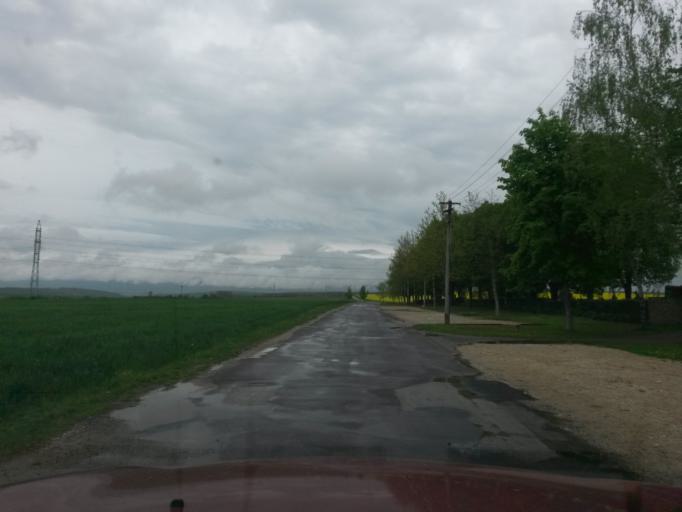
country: SK
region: Kosicky
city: Moldava nad Bodvou
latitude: 48.6014
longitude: 21.0204
